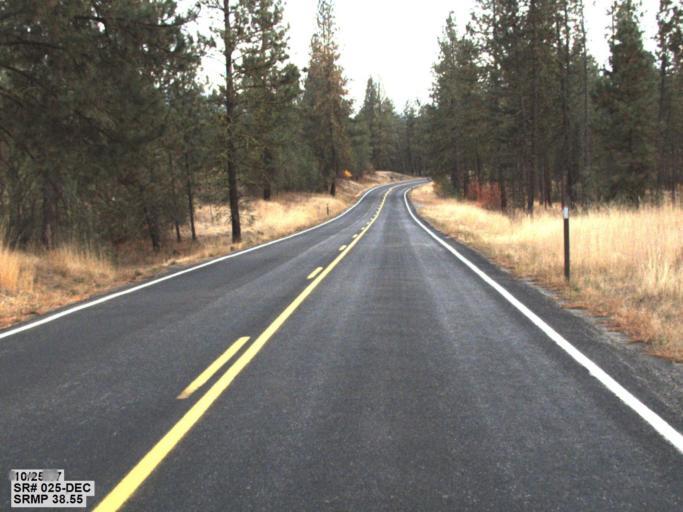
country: US
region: Washington
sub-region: Lincoln County
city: Davenport
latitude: 48.0775
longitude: -118.1982
